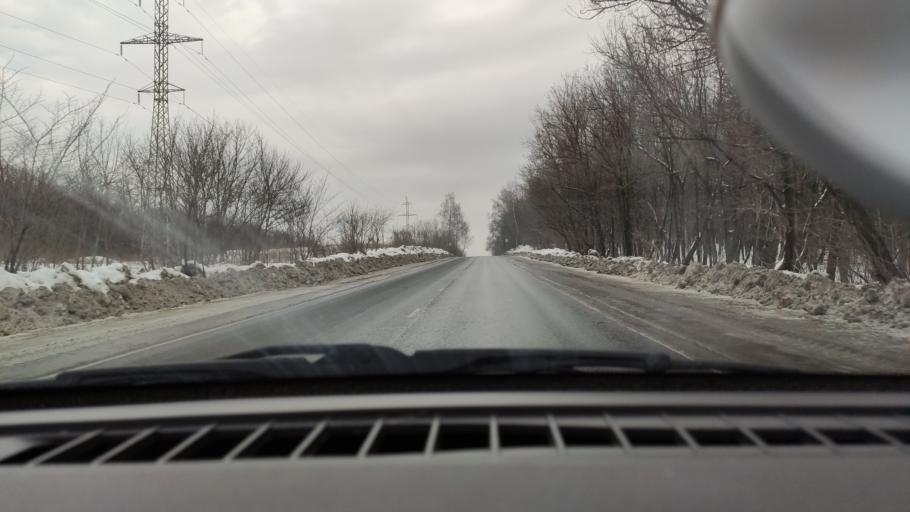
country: RU
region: Samara
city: Novosemeykino
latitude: 53.3426
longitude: 50.2463
